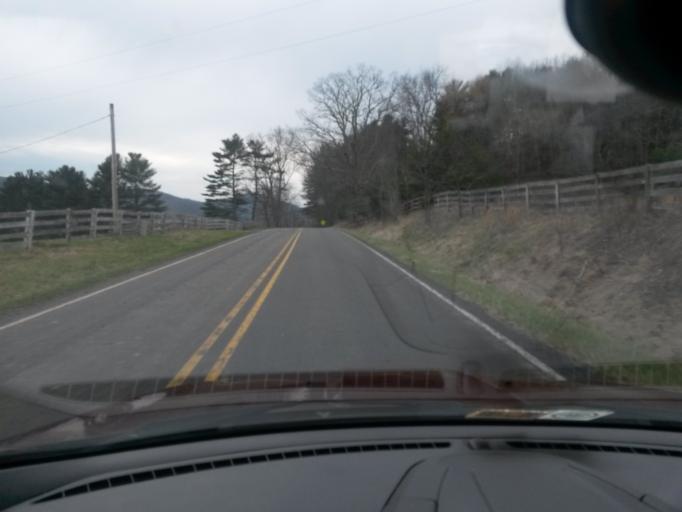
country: US
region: Virginia
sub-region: Bath County
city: Warm Springs
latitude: 38.2057
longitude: -79.7248
